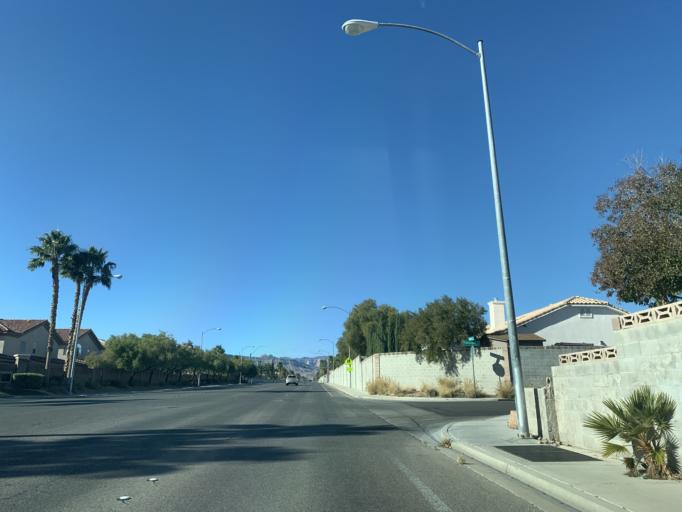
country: US
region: Nevada
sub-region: Clark County
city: Spring Valley
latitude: 36.1224
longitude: -115.2859
